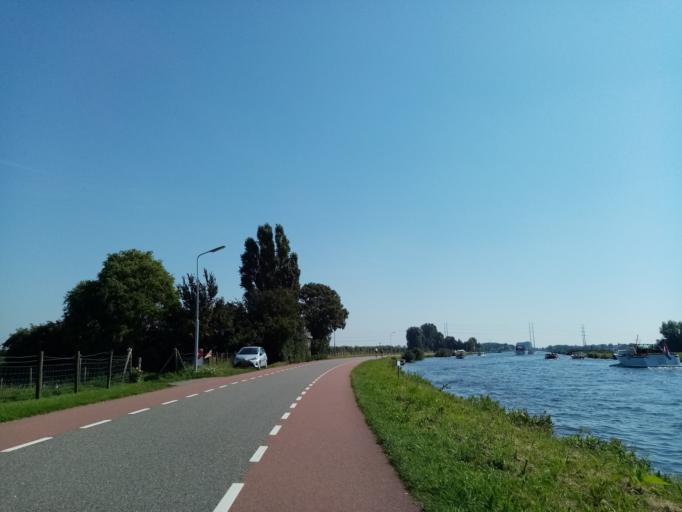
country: NL
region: South Holland
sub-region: Gemeente Lisse
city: Lisse
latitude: 52.2193
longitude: 4.5827
